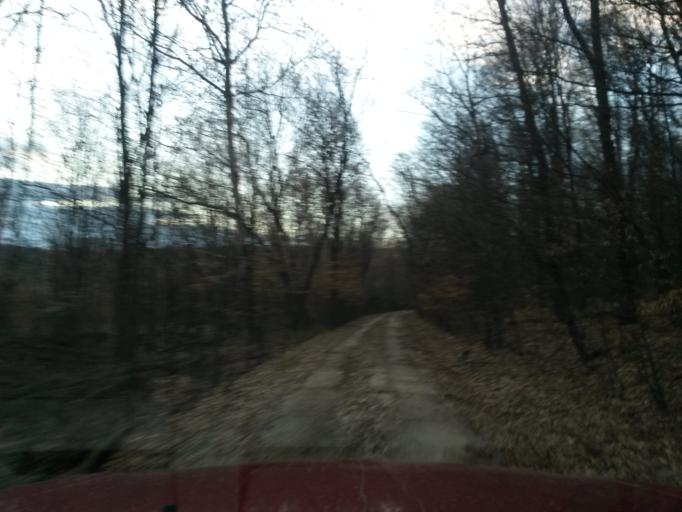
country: SK
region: Kosicky
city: Kosice
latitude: 48.6931
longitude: 21.3061
